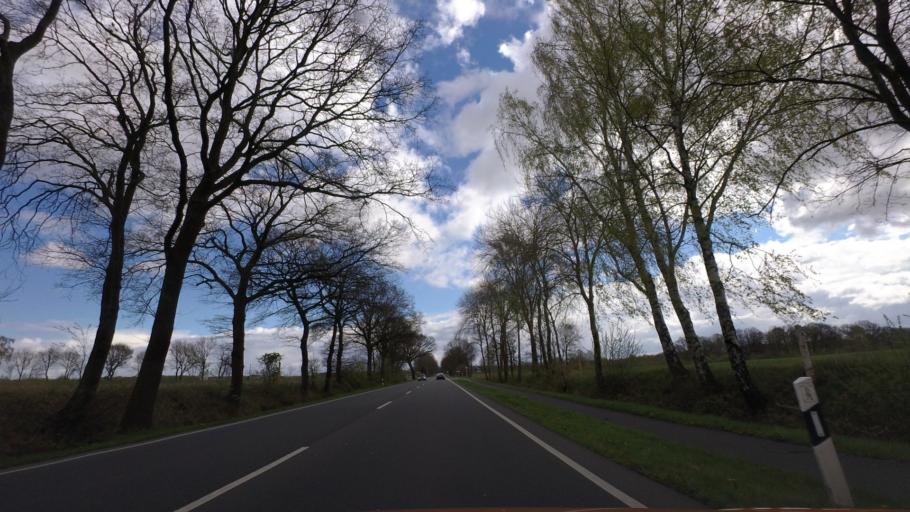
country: DE
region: Lower Saxony
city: Botersen
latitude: 53.1200
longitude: 9.2996
